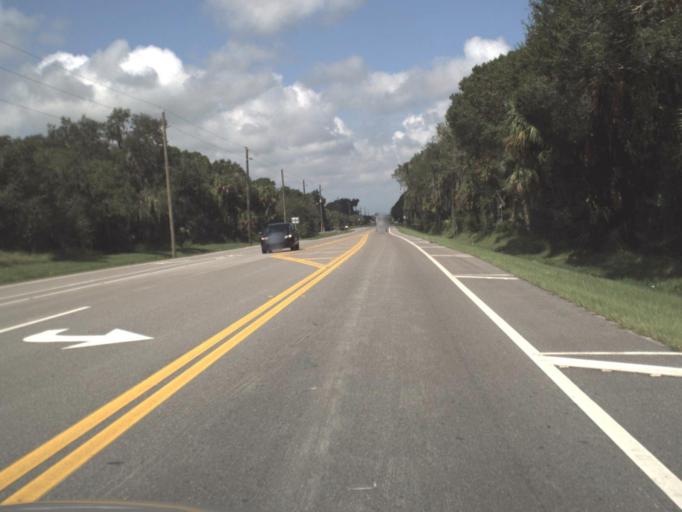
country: US
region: Florida
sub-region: Sarasota County
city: Lake Sarasota
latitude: 27.2481
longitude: -82.3821
